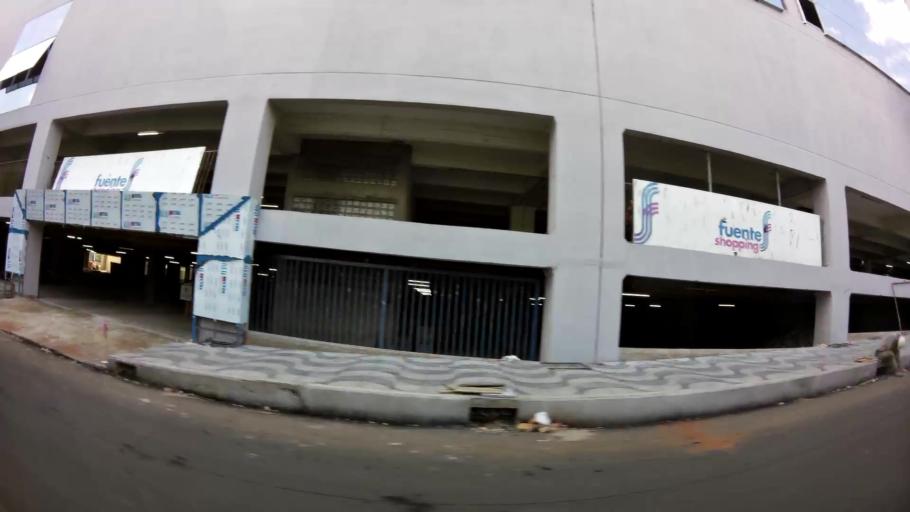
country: PY
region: Central
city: Fernando de la Mora
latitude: -25.3350
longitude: -57.5362
